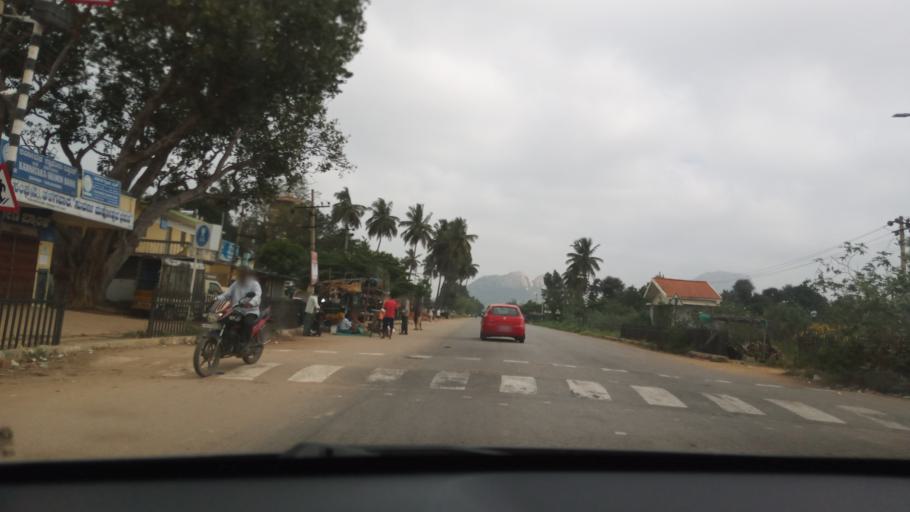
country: IN
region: Karnataka
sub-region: Chikkaballapur
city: Chintamani
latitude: 13.3177
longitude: 77.9815
